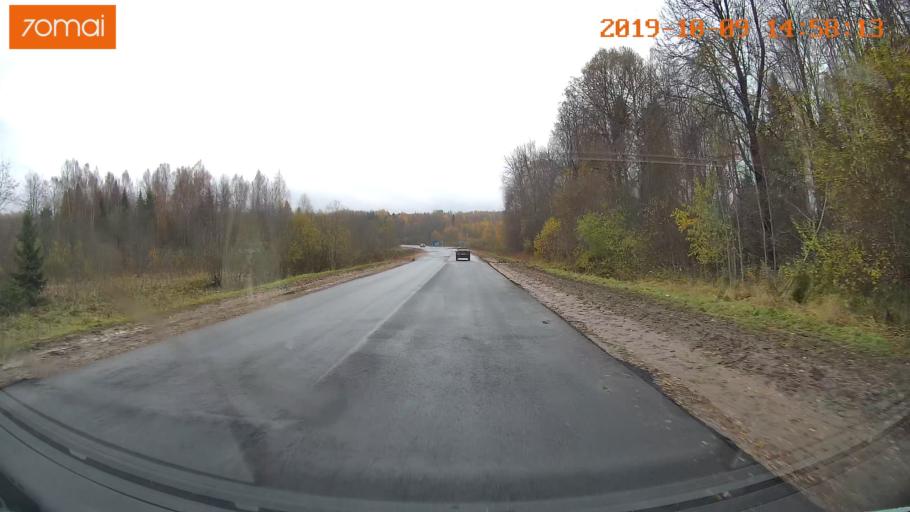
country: RU
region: Kostroma
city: Chistyye Bory
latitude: 58.3291
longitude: 41.6539
